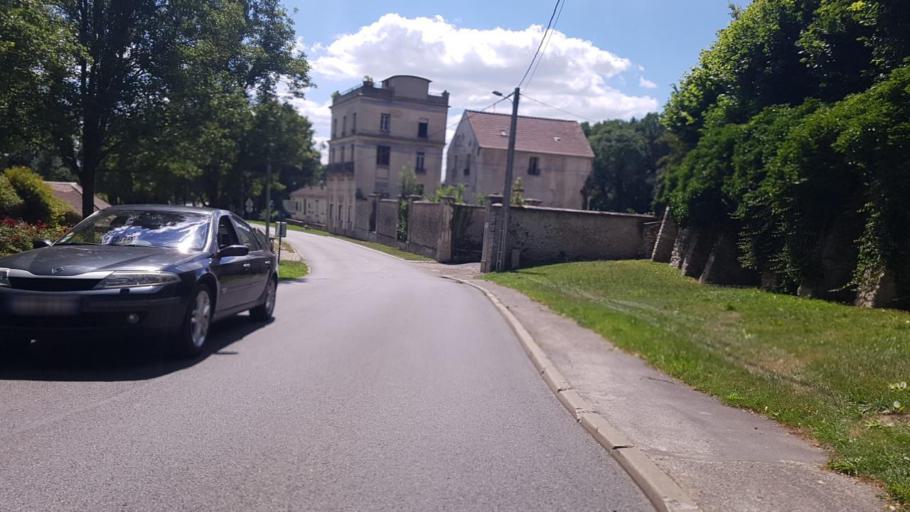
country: FR
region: Ile-de-France
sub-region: Departement de Seine-et-Marne
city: Longperrier
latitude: 49.0100
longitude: 2.6636
